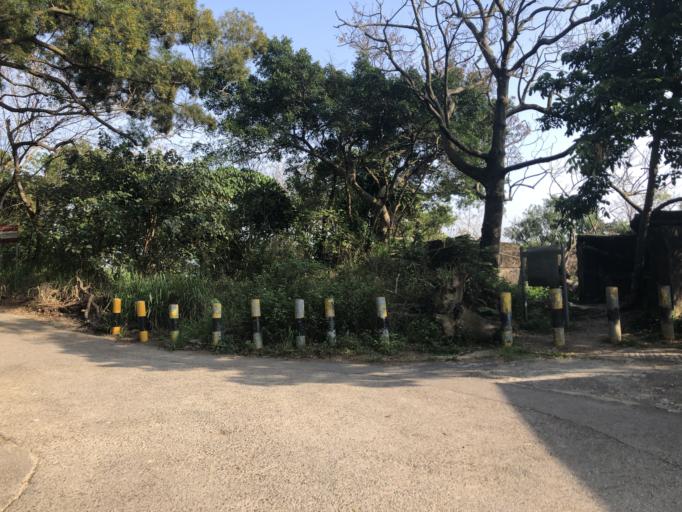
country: HK
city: Hong Kong
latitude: 22.2759
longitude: 114.1204
